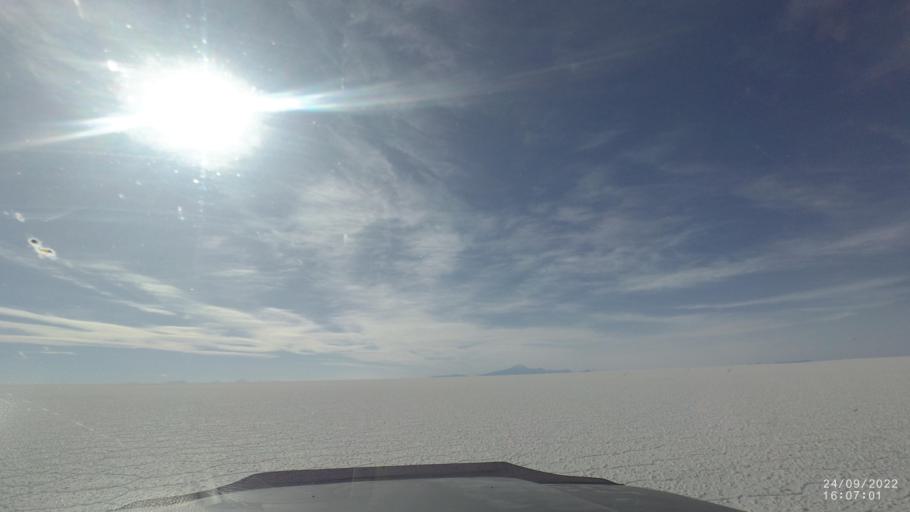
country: BO
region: Potosi
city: Colchani
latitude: -20.3023
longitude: -67.2990
